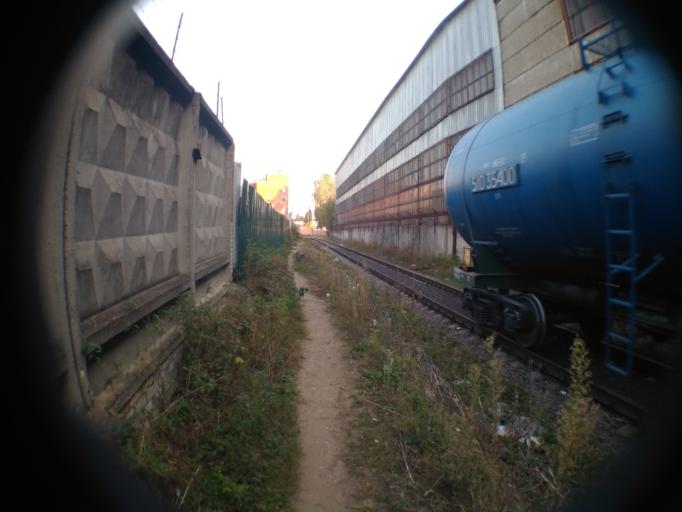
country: RU
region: Moskovskaya
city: Zhukovskiy
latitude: 55.5812
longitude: 38.1102
